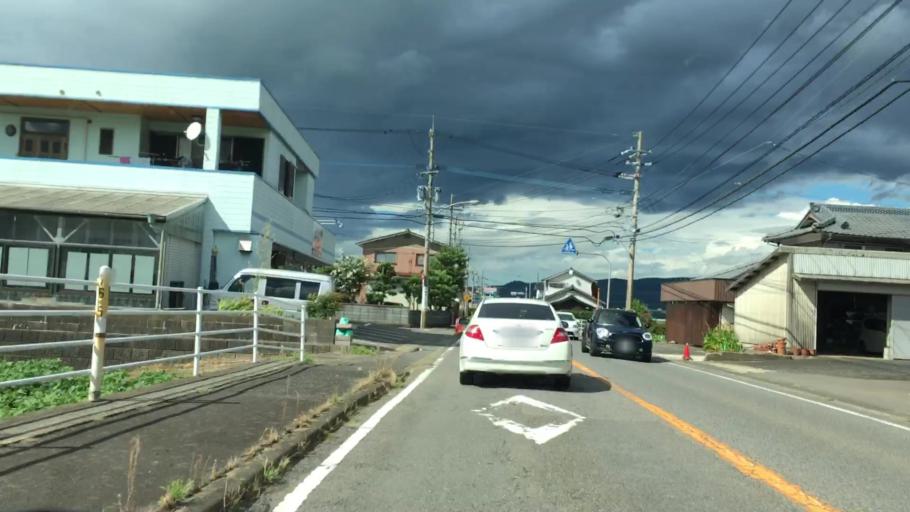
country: JP
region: Saga Prefecture
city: Imaricho-ko
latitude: 33.2499
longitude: 129.8527
